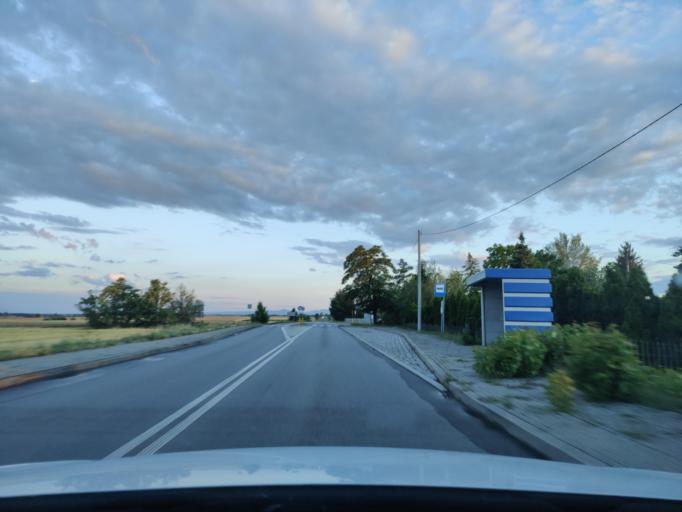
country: PL
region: Opole Voivodeship
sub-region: Powiat nyski
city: Chroscina
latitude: 50.6169
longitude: 17.3821
